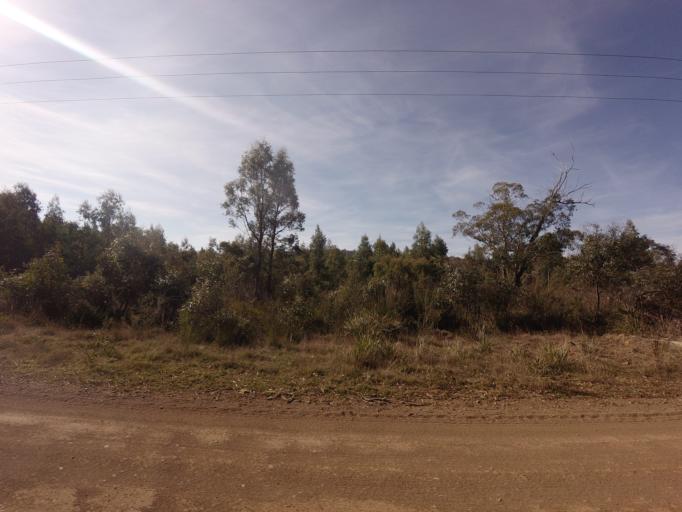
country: AU
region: Tasmania
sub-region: Sorell
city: Sorell
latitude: -42.4972
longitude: 147.5296
